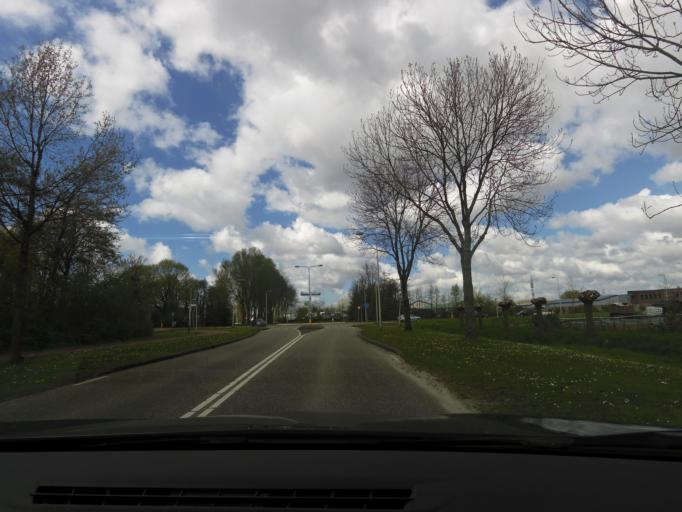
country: NL
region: South Holland
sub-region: Gemeente Albrandswaard
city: Rhoon
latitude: 51.8586
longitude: 4.4339
